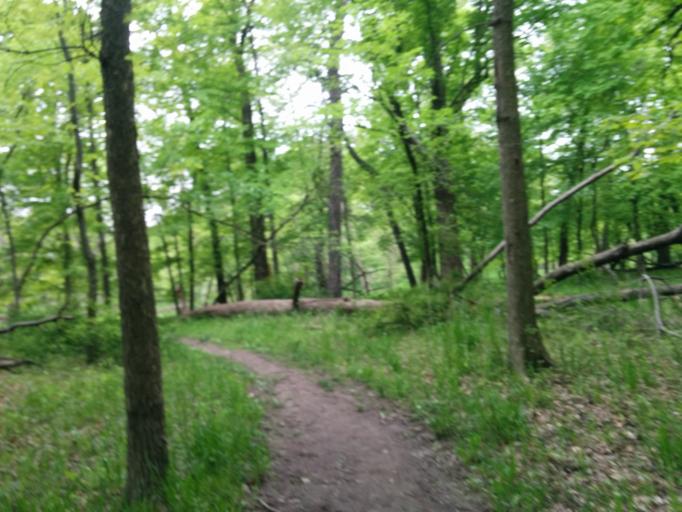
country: US
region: Illinois
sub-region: Cook County
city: Franklin Park
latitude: 41.9481
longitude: -87.8530
